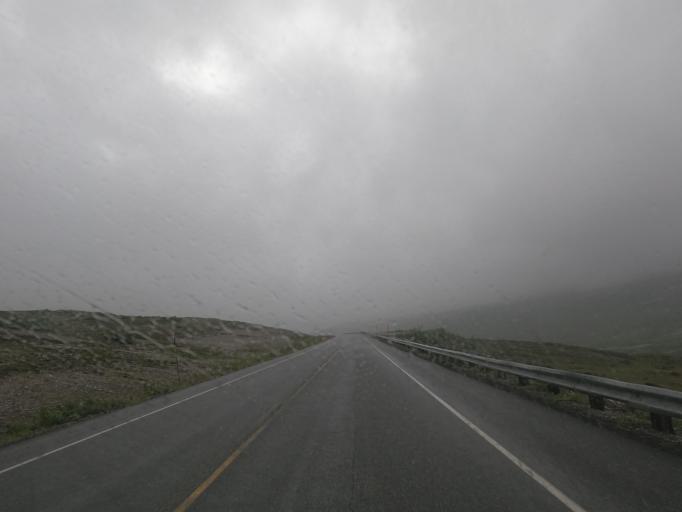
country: US
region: Alaska
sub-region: Haines Borough
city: Haines
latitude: 59.6703
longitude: -136.5595
